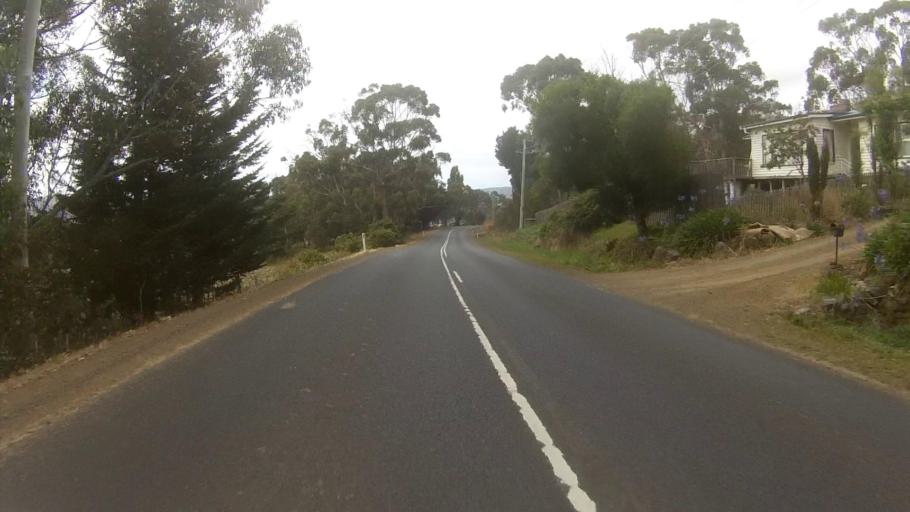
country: AU
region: Tasmania
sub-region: Kingborough
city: Margate
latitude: -43.0174
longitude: 147.2526
